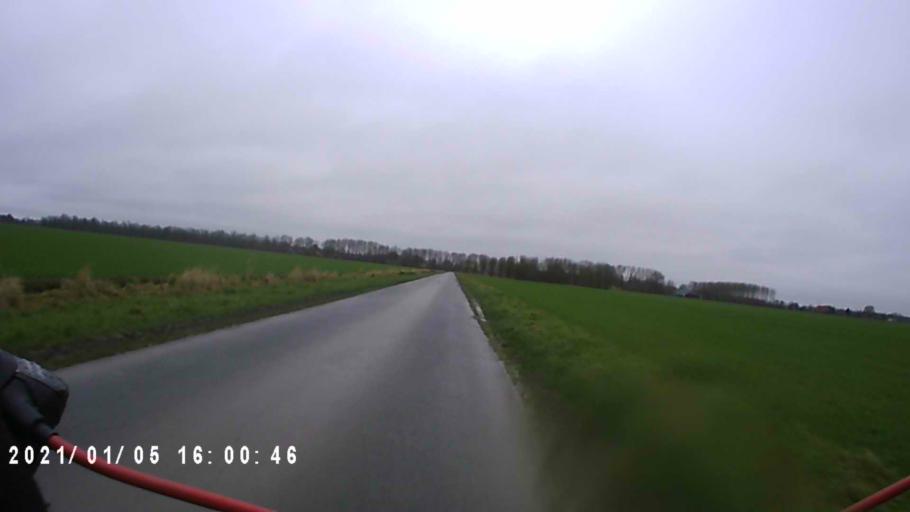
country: NL
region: Groningen
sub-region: Gemeente  Oldambt
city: Winschoten
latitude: 53.2057
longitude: 7.0828
